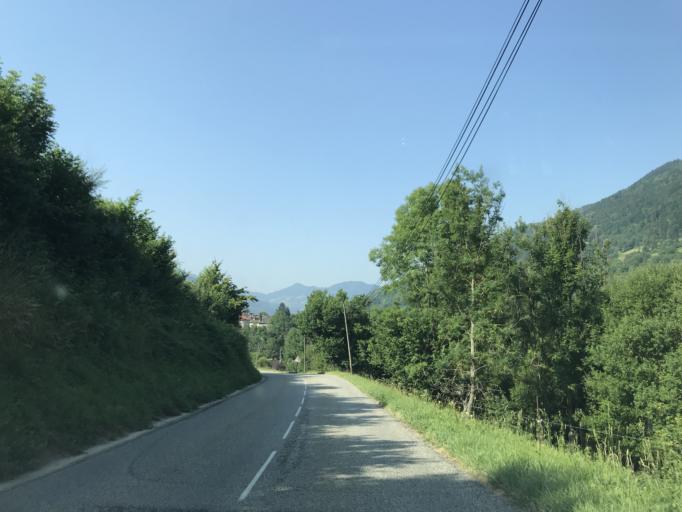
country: FR
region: Rhone-Alpes
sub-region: Departement de l'Isere
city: Allevard
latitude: 45.4266
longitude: 6.0981
